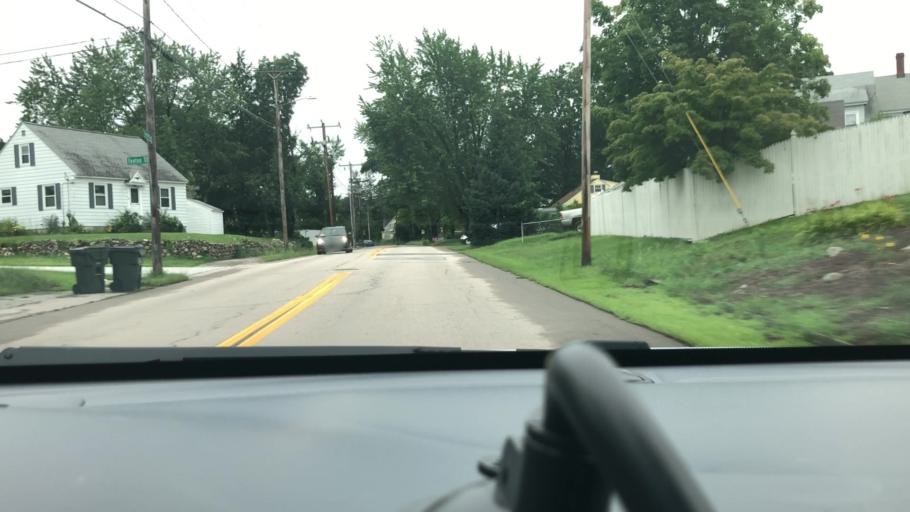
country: US
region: New Hampshire
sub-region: Hillsborough County
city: Pinardville
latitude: 42.9789
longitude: -71.4904
